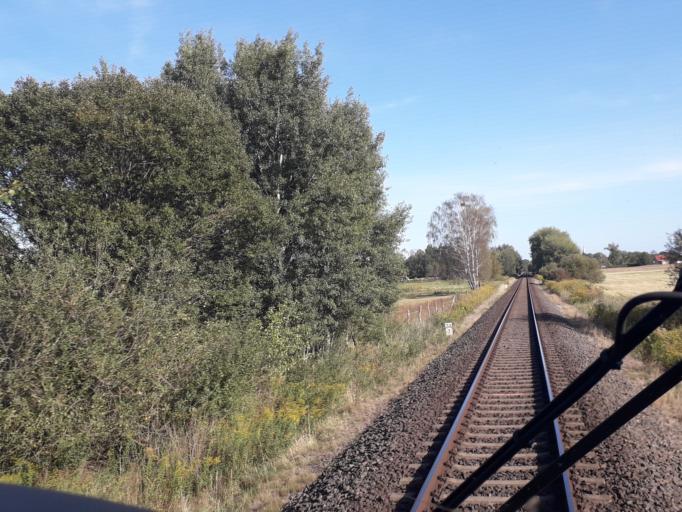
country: DE
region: Brandenburg
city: Kremmen
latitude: 52.7417
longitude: 13.0698
